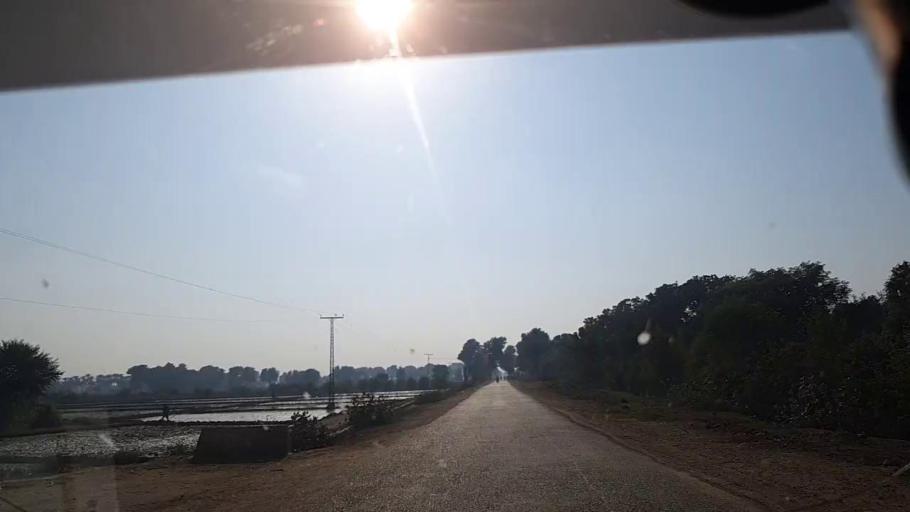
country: PK
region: Sindh
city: Sobhadero
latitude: 27.2487
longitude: 68.2943
